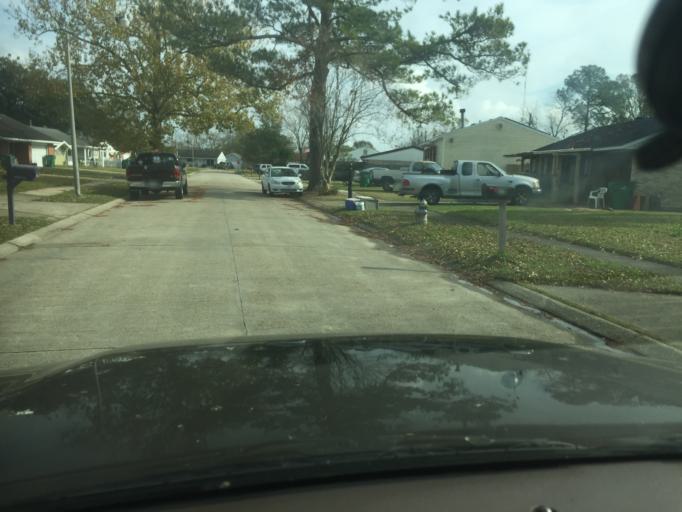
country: US
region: Louisiana
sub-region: Jefferson Parish
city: Avondale
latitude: 29.9145
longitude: -90.2026
